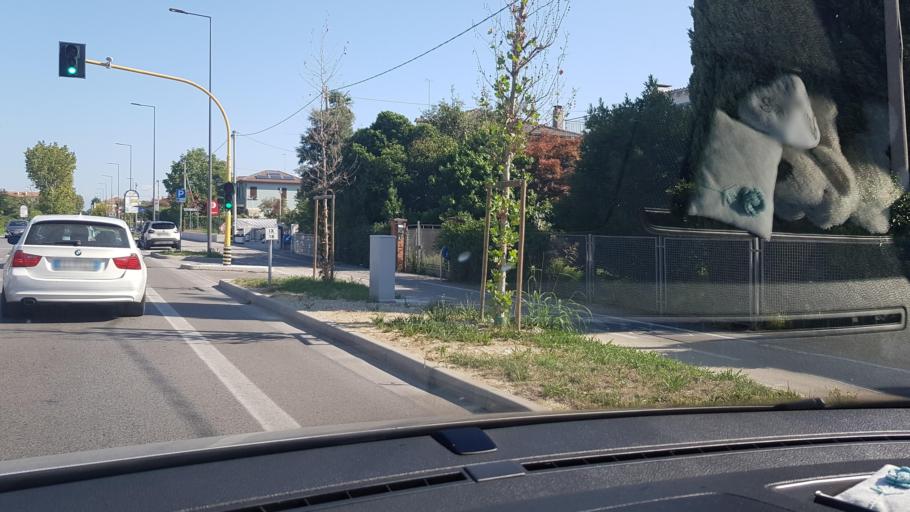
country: IT
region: Veneto
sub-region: Provincia di Treviso
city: Frescada
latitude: 45.6399
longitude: 12.2406
